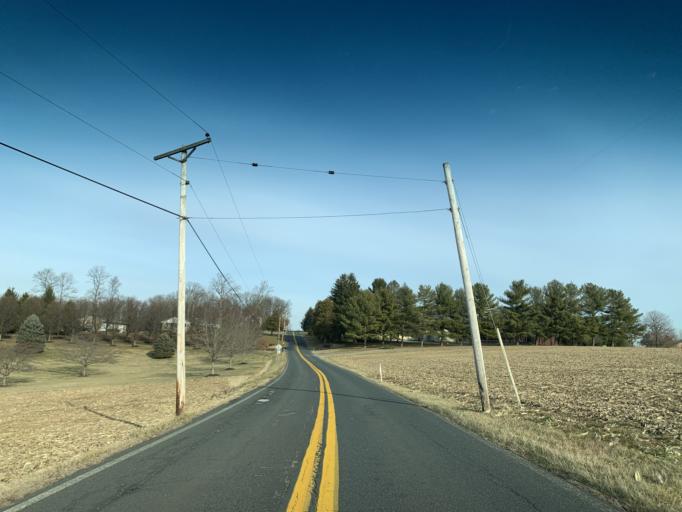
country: US
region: Maryland
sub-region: Carroll County
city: Hampstead
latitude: 39.5973
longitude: -76.8757
